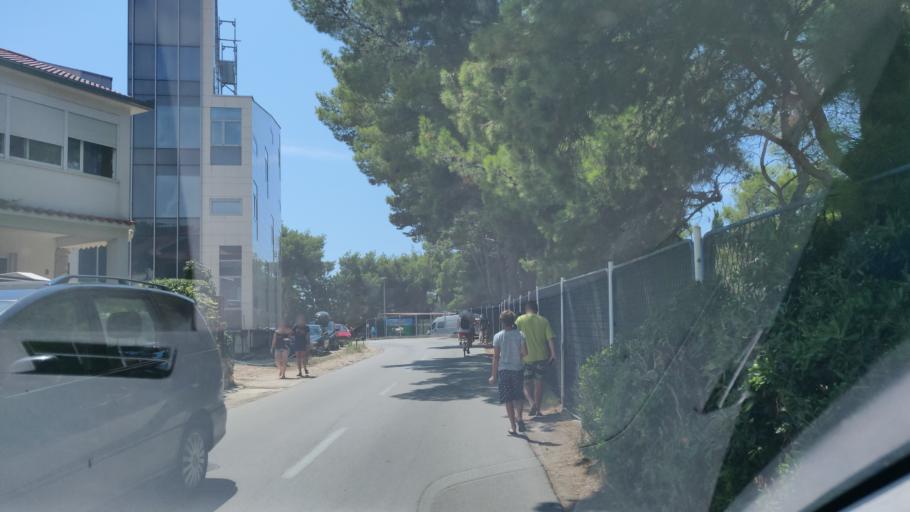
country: HR
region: Splitsko-Dalmatinska
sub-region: Grad Trogir
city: Trogir
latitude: 43.5057
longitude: 16.2588
